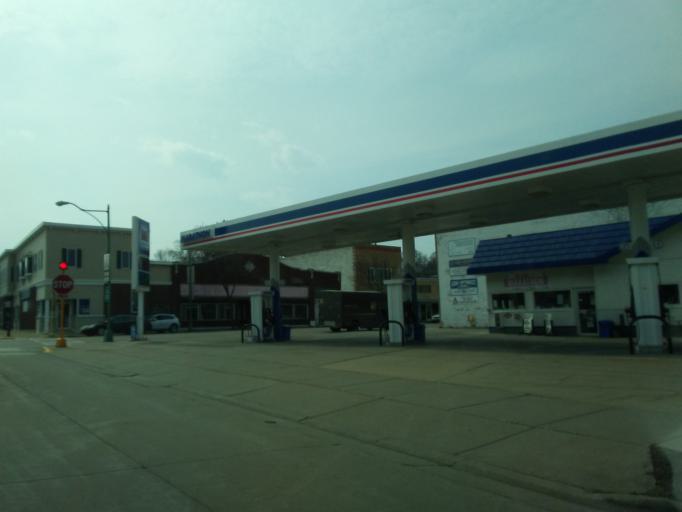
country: US
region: Wisconsin
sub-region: Columbia County
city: Lodi
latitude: 43.3142
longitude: -89.5270
